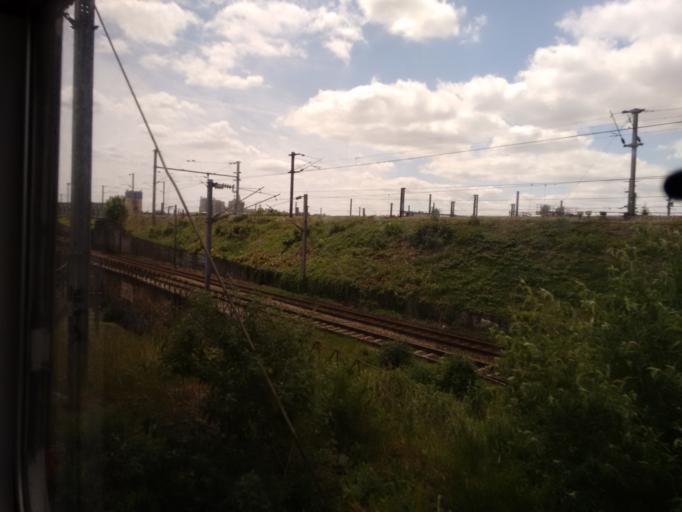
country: FR
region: Ile-de-France
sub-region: Paris
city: Saint-Ouen
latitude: 48.9079
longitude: 2.3529
